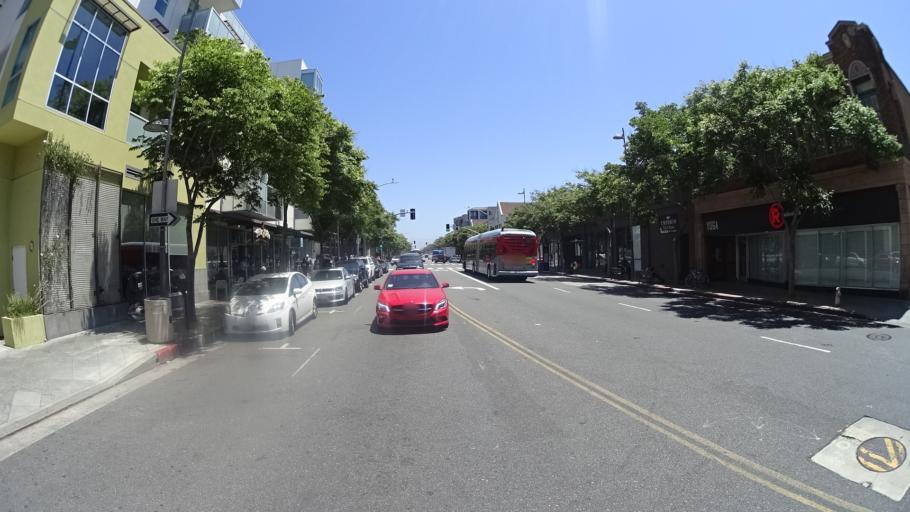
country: US
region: California
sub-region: Los Angeles County
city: Santa Monica
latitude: 34.0176
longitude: -118.4938
